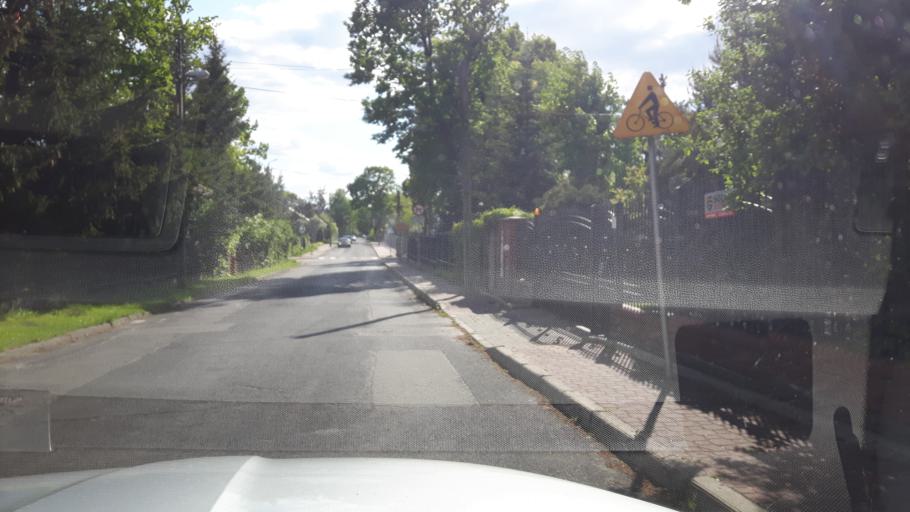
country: PL
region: Masovian Voivodeship
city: Zielonka
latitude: 52.3070
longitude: 21.1544
